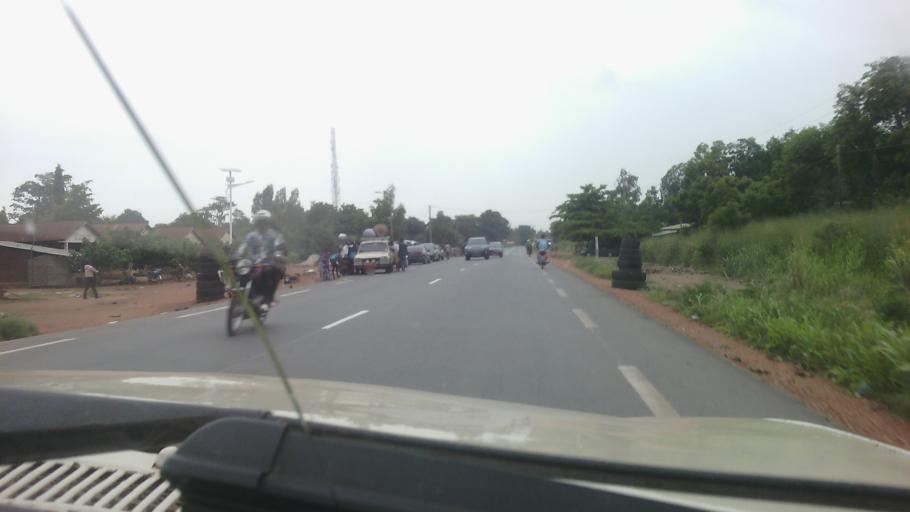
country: BJ
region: Mono
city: Come
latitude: 6.4010
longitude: 1.9599
